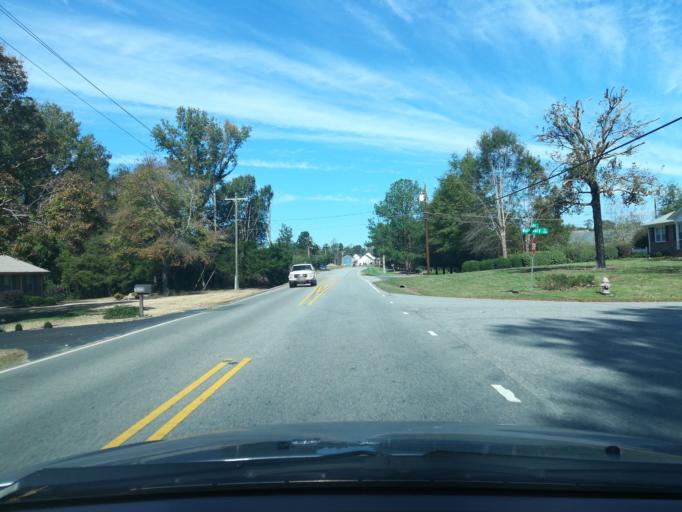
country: US
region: North Carolina
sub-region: Durham County
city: Durham
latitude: 35.9684
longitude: -78.9767
